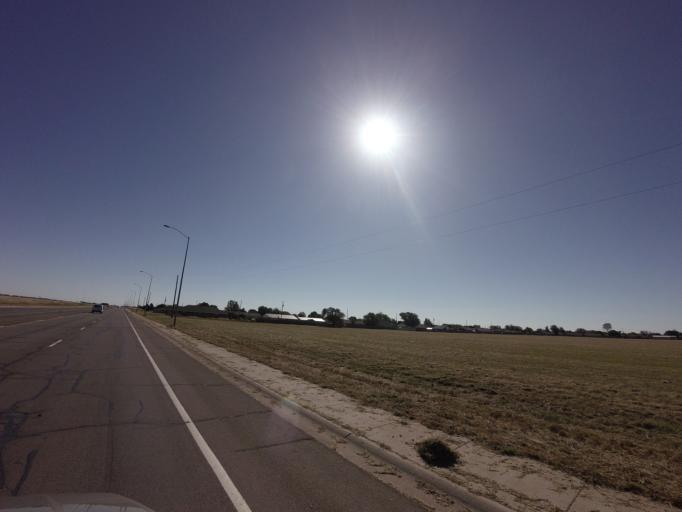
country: US
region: New Mexico
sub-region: Curry County
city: Clovis
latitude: 34.4340
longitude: -103.2285
